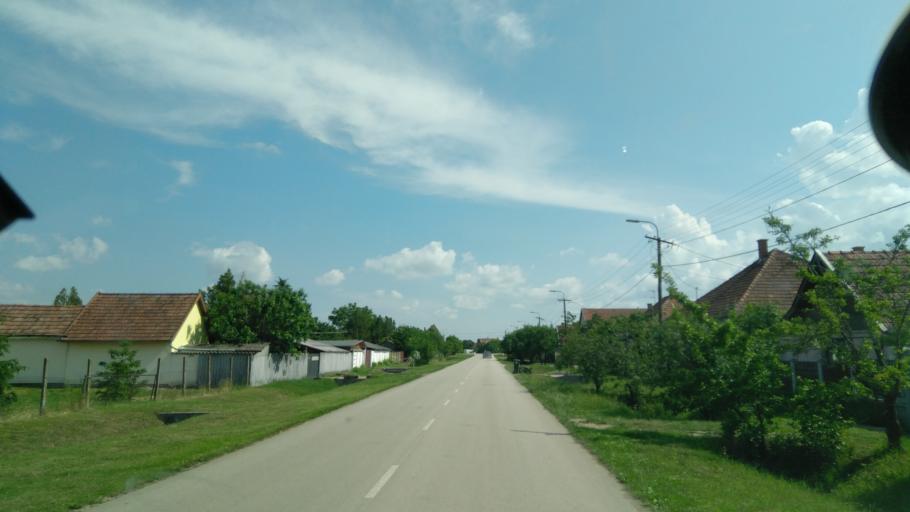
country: HU
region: Bekes
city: Doboz
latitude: 46.7353
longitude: 21.2376
